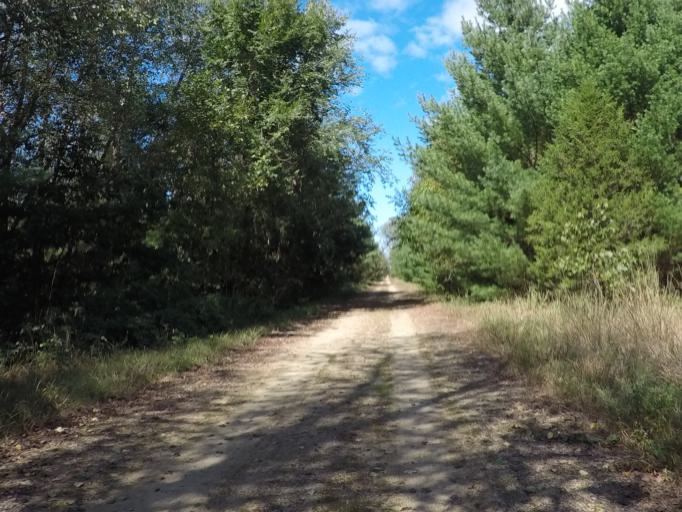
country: US
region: Wisconsin
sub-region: Sauk County
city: Spring Green
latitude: 43.1863
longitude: -90.2134
